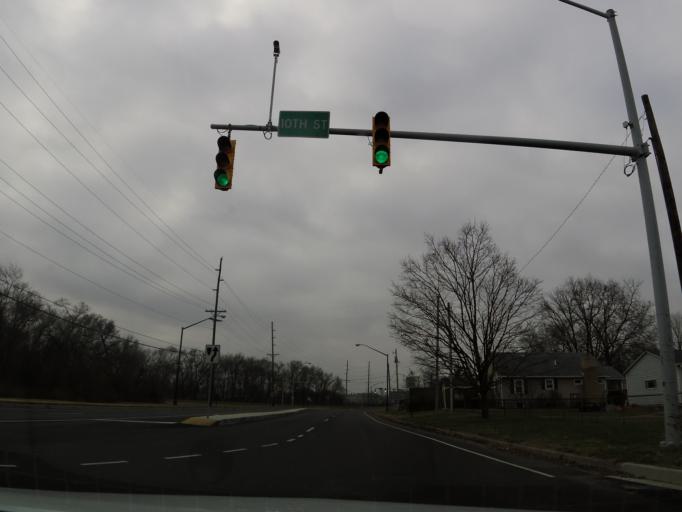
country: US
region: Indiana
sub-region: Bartholomew County
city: Columbus
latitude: 39.2086
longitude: -85.9041
